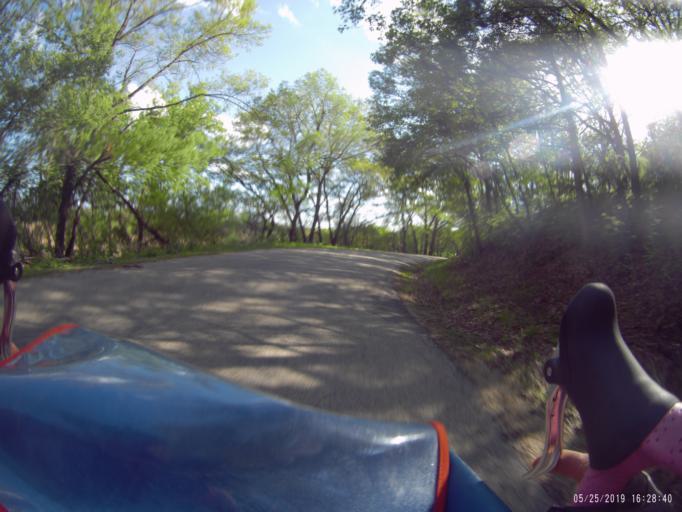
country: US
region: Wisconsin
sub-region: Dane County
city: Mount Horeb
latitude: 42.9461
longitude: -89.7081
